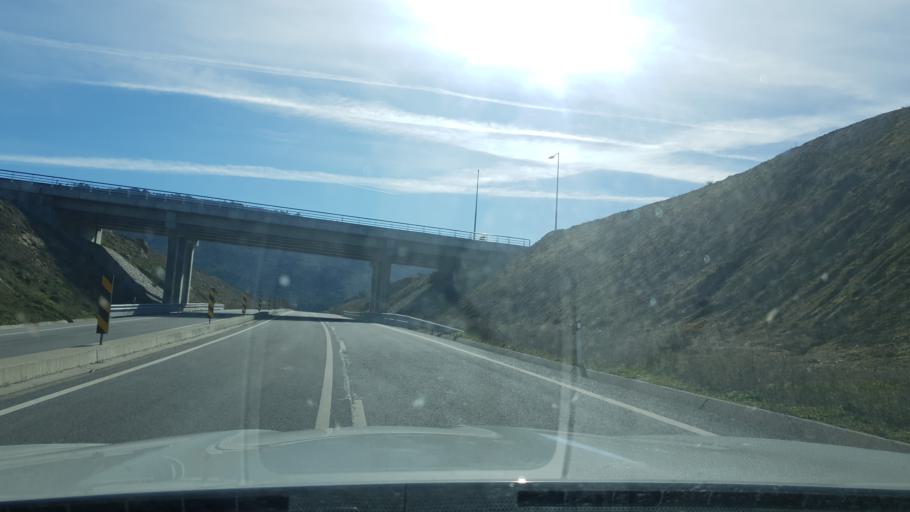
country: PT
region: Braganca
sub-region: Carrazeda de Ansiaes
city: Carrazeda de Anciaes
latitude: 41.3037
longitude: -7.3423
